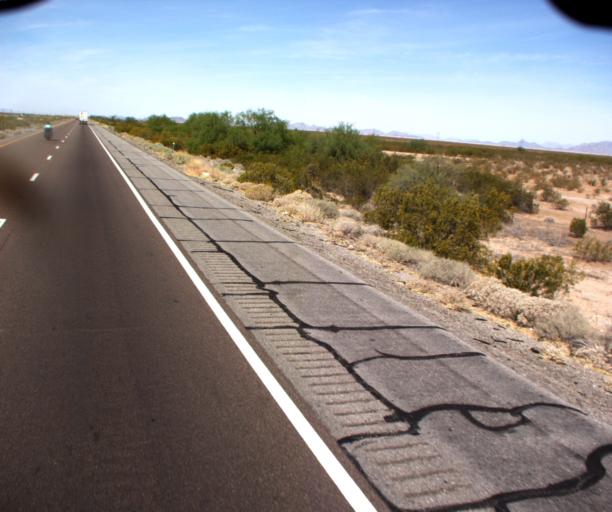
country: US
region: Arizona
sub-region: La Paz County
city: Salome
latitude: 33.5626
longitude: -113.3089
